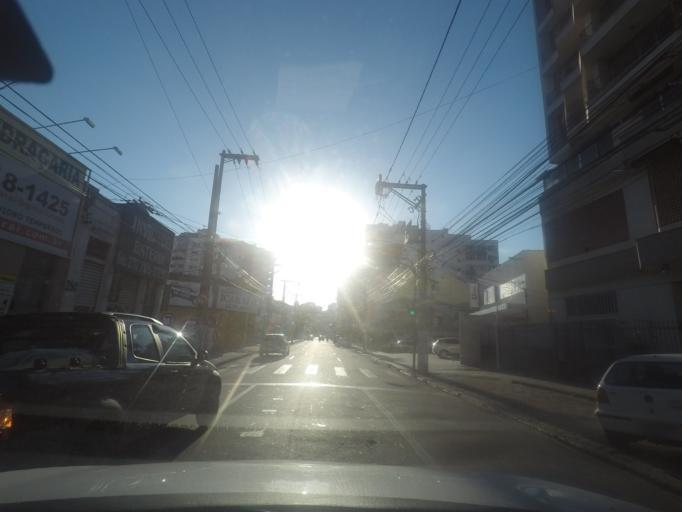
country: BR
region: Rio de Janeiro
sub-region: Niteroi
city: Niteroi
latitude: -22.8988
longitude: -43.1057
